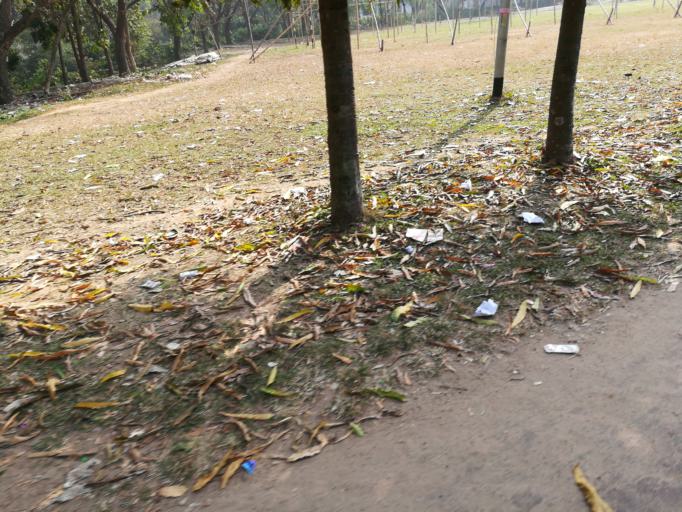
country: BD
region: Chittagong
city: Chittagong
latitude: 22.4738
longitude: 91.7856
